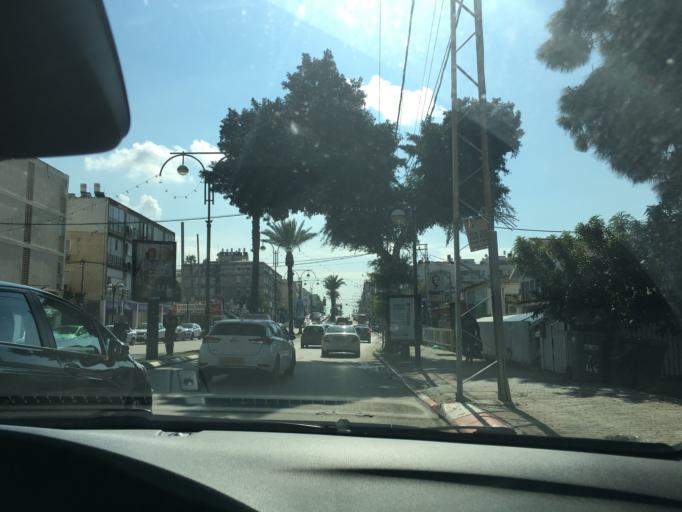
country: IL
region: Tel Aviv
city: Ramat HaSharon
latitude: 32.1471
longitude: 34.8391
